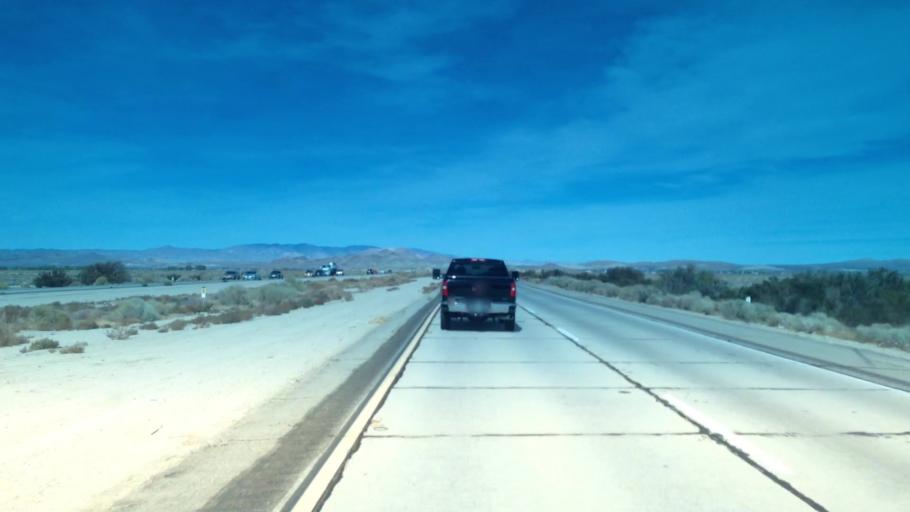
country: US
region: California
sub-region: Kern County
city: Rosamond
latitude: 34.7931
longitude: -118.1706
